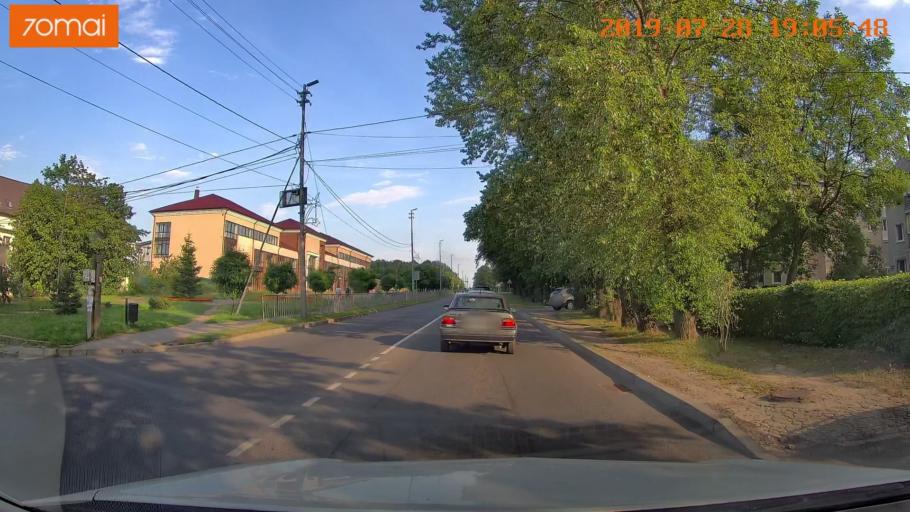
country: RU
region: Kaliningrad
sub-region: Gorod Svetlogorsk
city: Svetlogorsk
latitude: 54.9321
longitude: 20.1638
